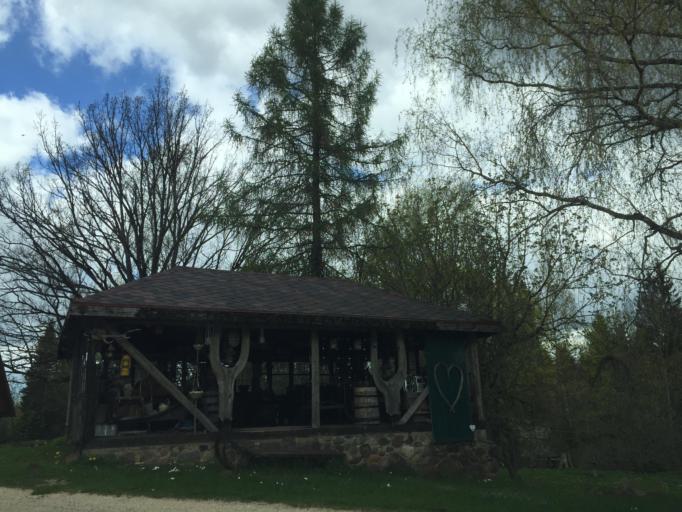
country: LV
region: Madonas Rajons
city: Madona
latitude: 56.9243
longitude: 26.0159
